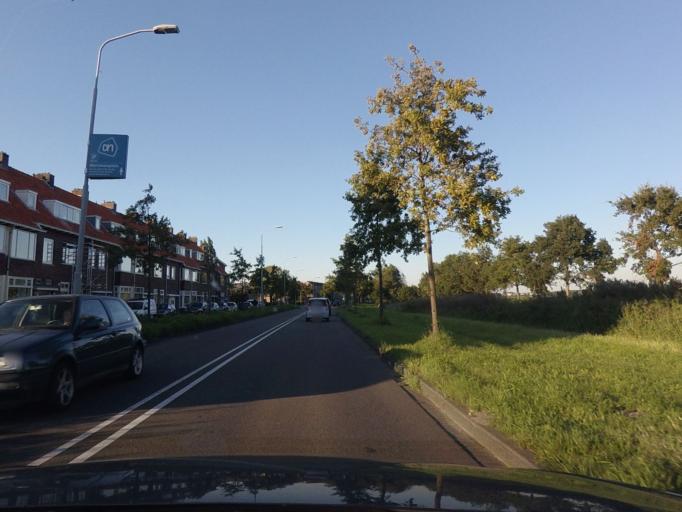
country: NL
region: North Holland
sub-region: Gemeente Bloemendaal
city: Bloemendaal
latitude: 52.4128
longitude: 4.6567
